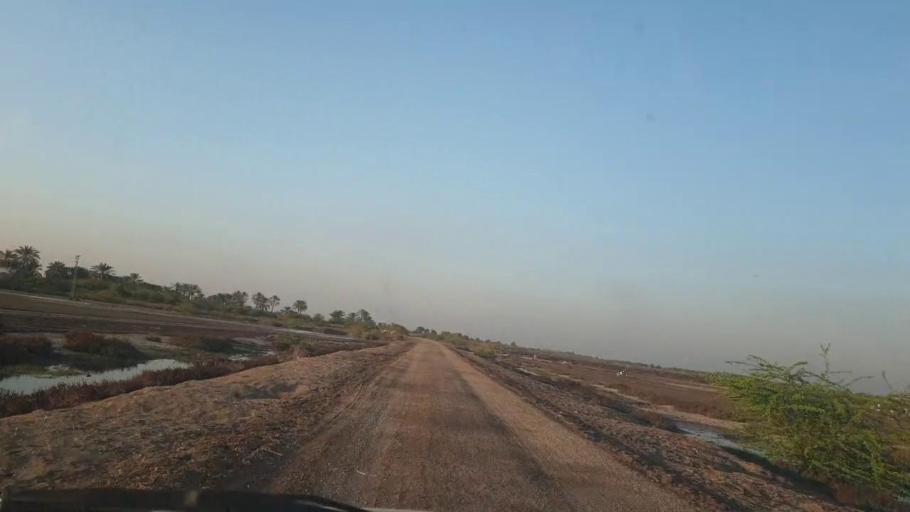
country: PK
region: Sindh
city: Mirpur Khas
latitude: 25.4464
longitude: 69.0798
